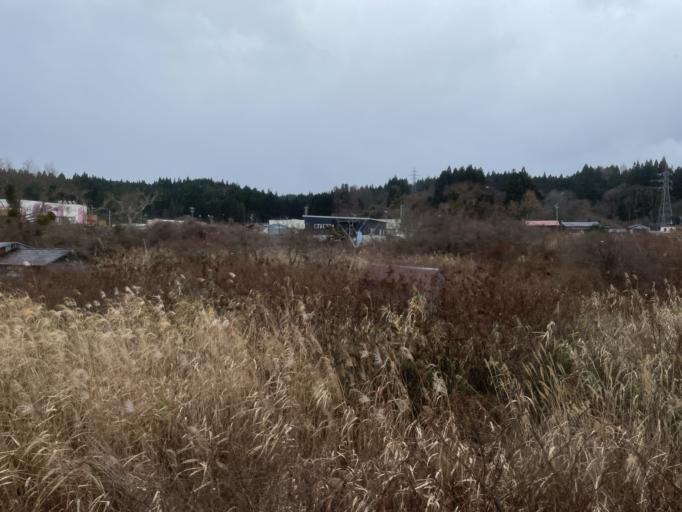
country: JP
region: Aomori
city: Goshogawara
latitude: 41.1783
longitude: 140.4922
